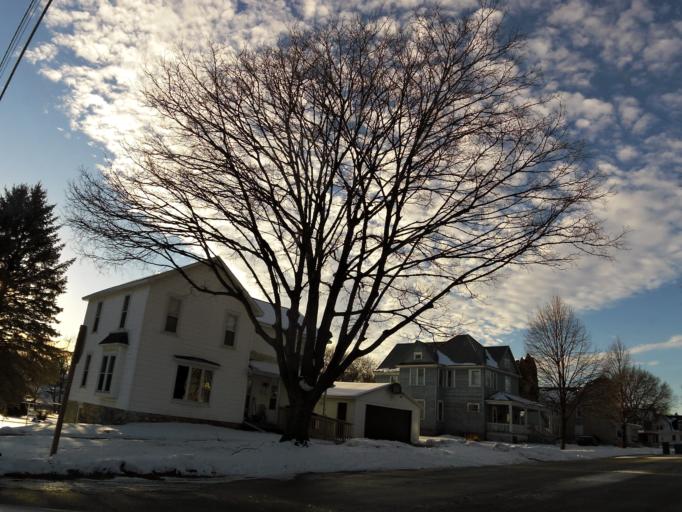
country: US
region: Iowa
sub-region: Butler County
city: Shell Rock
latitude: 42.7087
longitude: -92.5831
